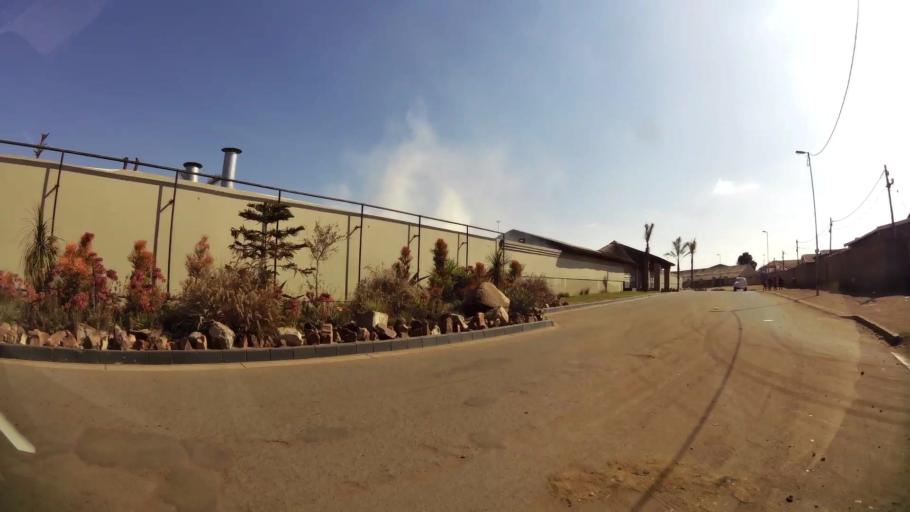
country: ZA
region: Gauteng
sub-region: City of Johannesburg Metropolitan Municipality
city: Soweto
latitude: -26.2899
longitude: 27.8542
